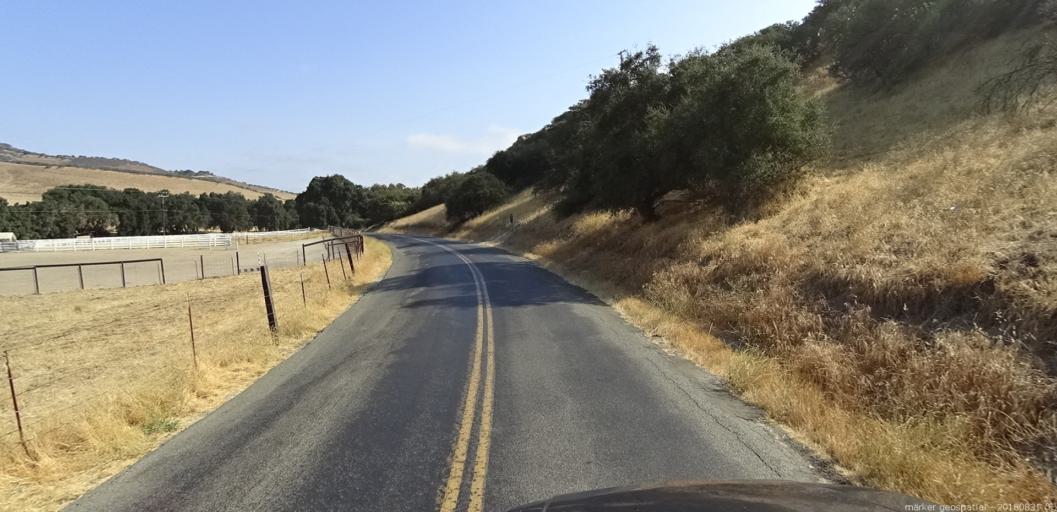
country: US
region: California
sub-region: Monterey County
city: King City
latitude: 36.1611
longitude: -121.1634
